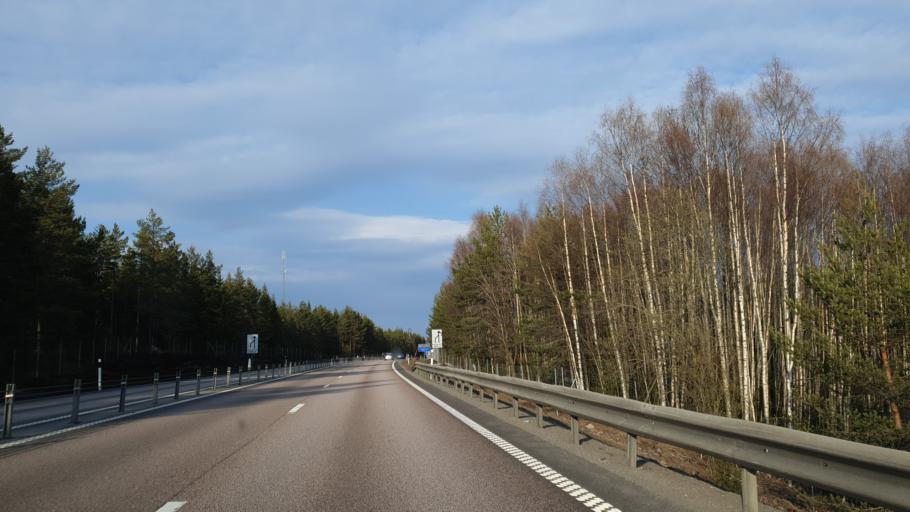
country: SE
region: Gaevleborg
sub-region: Hudiksvalls Kommun
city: Hudiksvall
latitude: 61.7744
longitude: 17.1099
